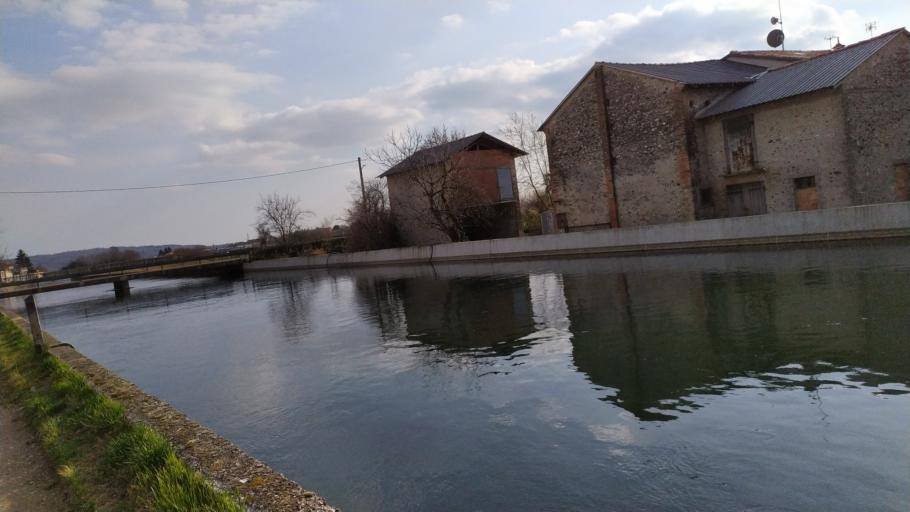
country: IT
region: Veneto
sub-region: Provincia di Treviso
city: Crocetta del Montello
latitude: 45.8442
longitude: 12.0214
